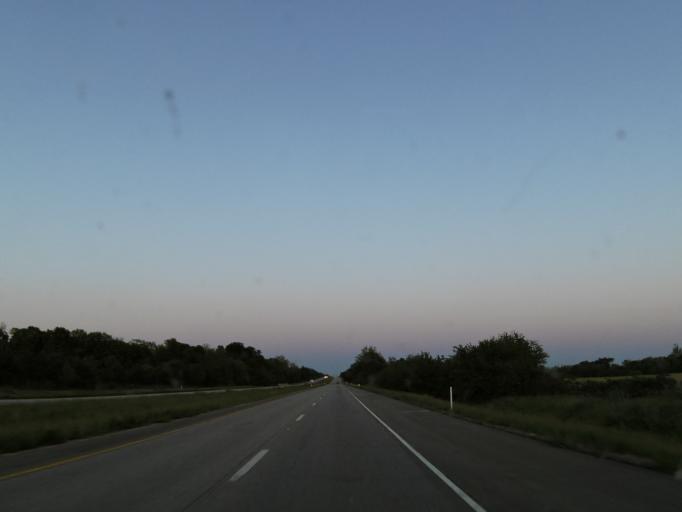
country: US
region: Indiana
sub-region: Montgomery County
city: Crawfordsville
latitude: 40.0003
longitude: -86.7334
